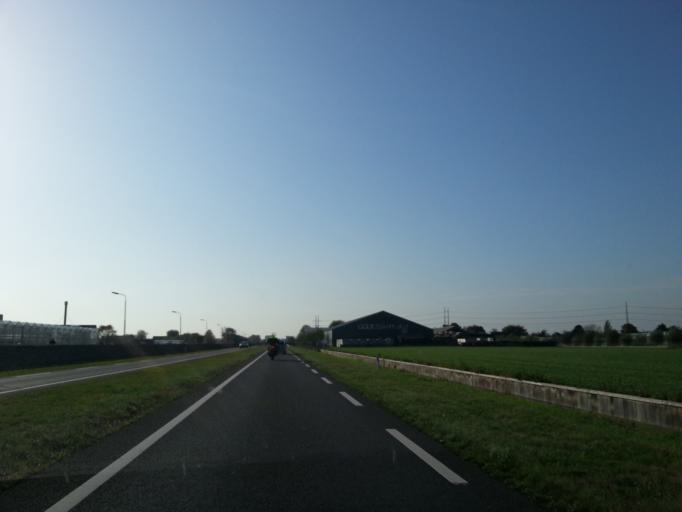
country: NL
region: South Holland
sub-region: Gemeente Lansingerland
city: Berkel en Rodenrijs
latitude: 52.0167
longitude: 4.4698
